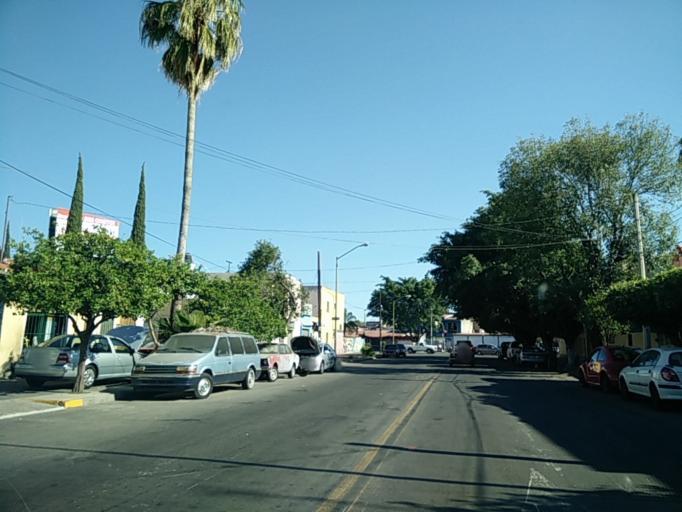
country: MX
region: Jalisco
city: Tlaquepaque
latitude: 20.6576
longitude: -103.3300
